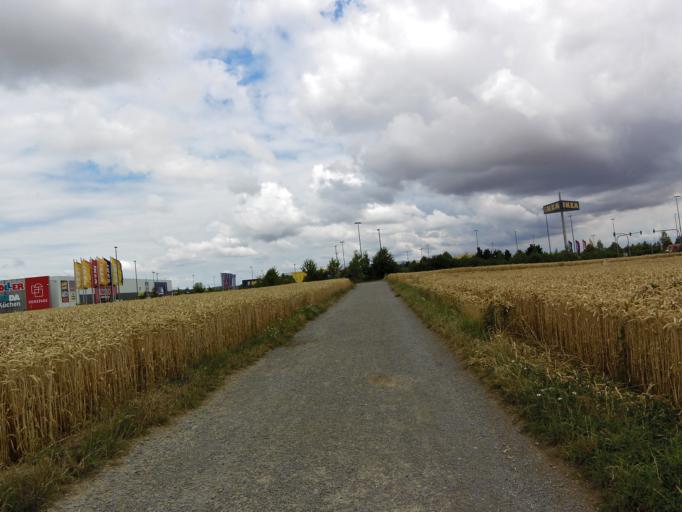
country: DE
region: Bavaria
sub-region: Regierungsbezirk Unterfranken
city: Estenfeld
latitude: 49.8193
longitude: 9.9798
